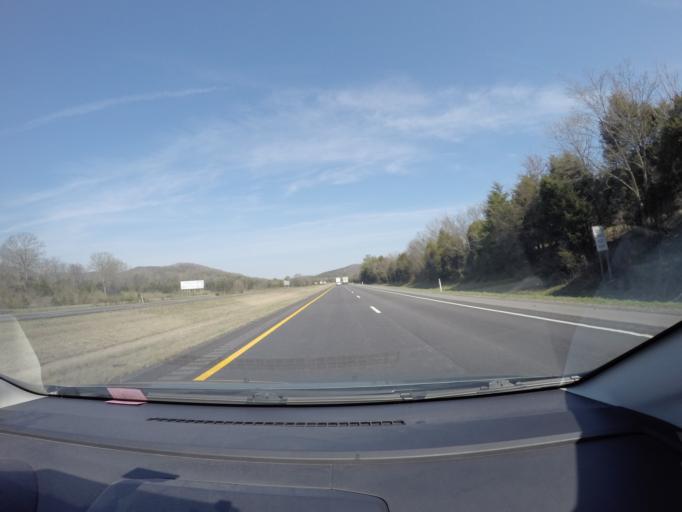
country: US
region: Tennessee
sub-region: Rutherford County
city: Plainview
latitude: 35.6410
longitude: -86.2506
